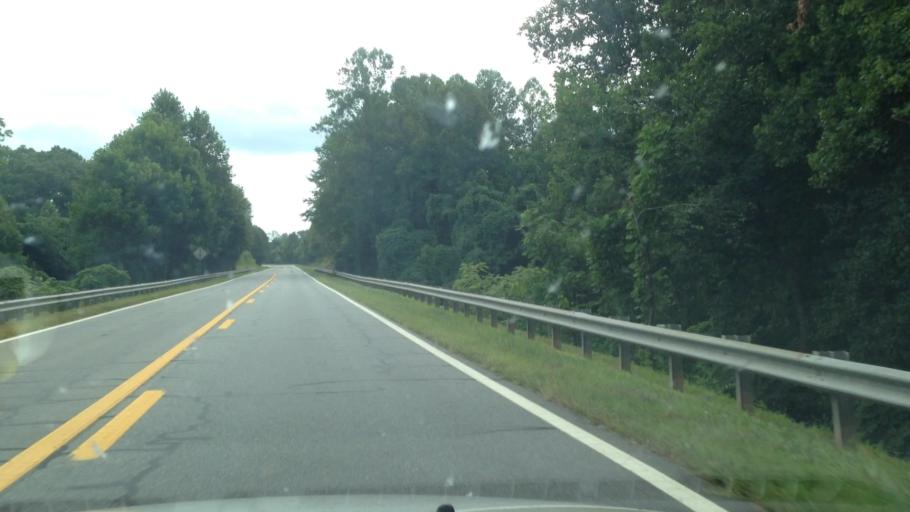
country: US
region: North Carolina
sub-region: Rockingham County
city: Wentworth
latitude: 36.3884
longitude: -79.8167
